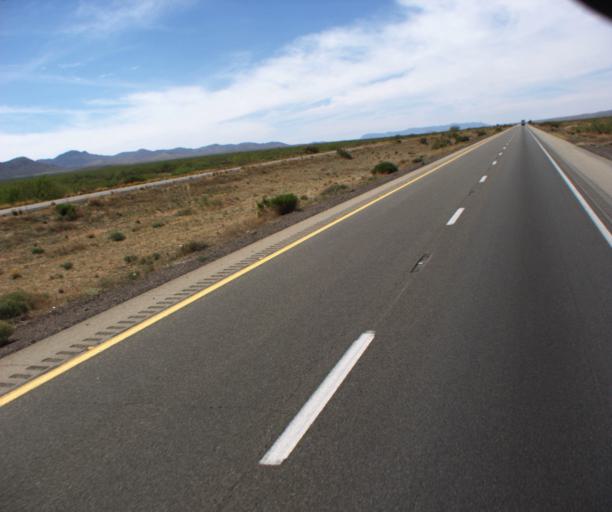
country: US
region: Arizona
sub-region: Cochise County
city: Willcox
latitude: 32.3383
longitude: -109.5501
